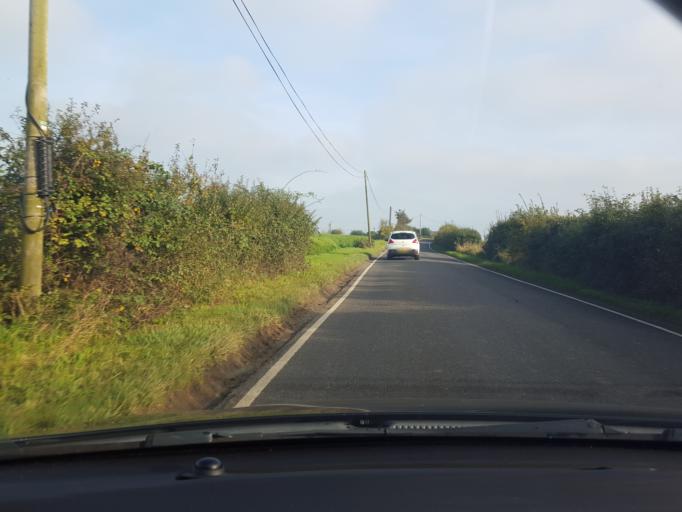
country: GB
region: England
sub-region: Essex
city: Little Clacton
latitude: 51.8620
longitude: 1.1875
